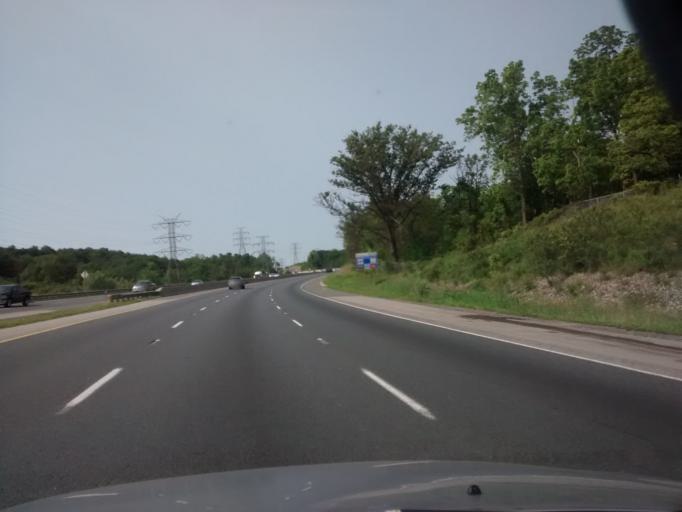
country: CA
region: Ontario
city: Hamilton
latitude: 43.2093
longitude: -79.8051
